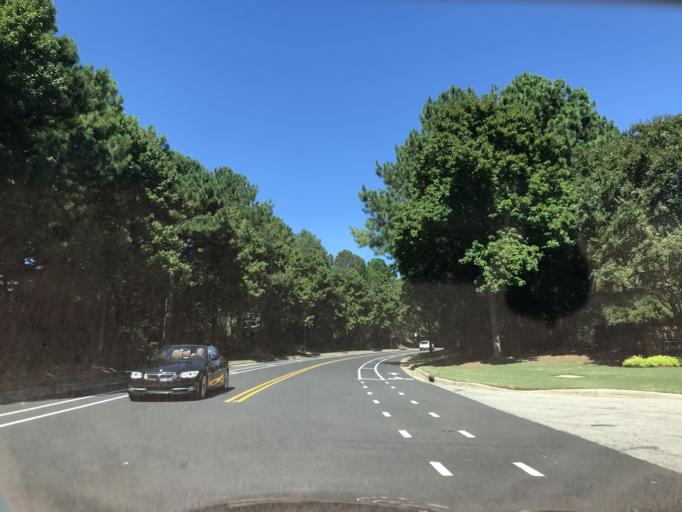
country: US
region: North Carolina
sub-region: Wake County
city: Wake Forest
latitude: 35.9498
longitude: -78.5638
